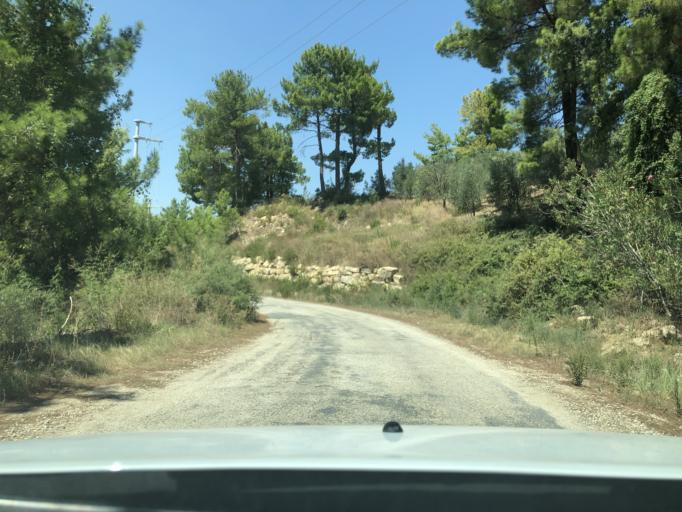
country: TR
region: Antalya
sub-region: Manavgat
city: Manavgat
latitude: 36.8717
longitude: 31.5526
